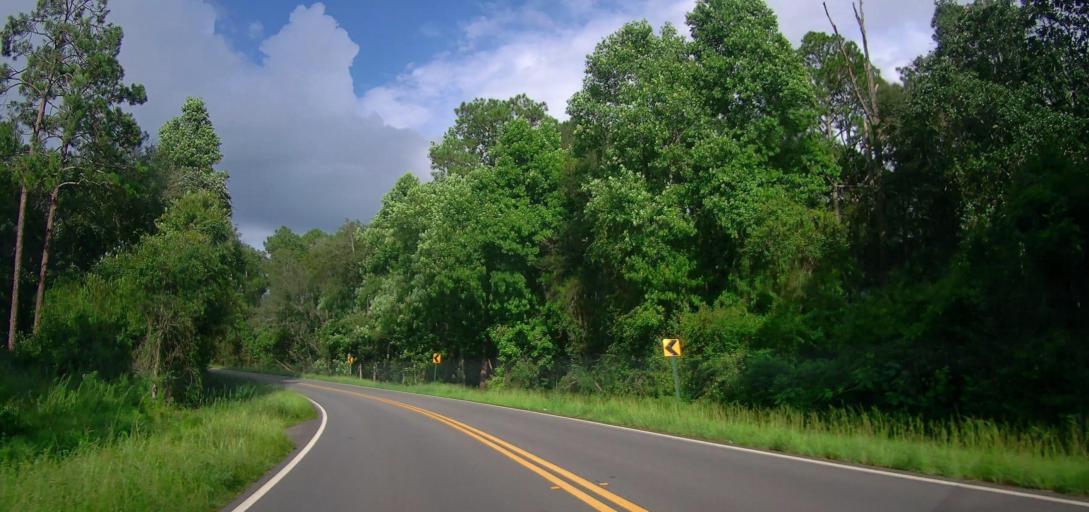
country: US
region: Georgia
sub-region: Coffee County
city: Douglas
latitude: 31.4485
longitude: -82.8691
